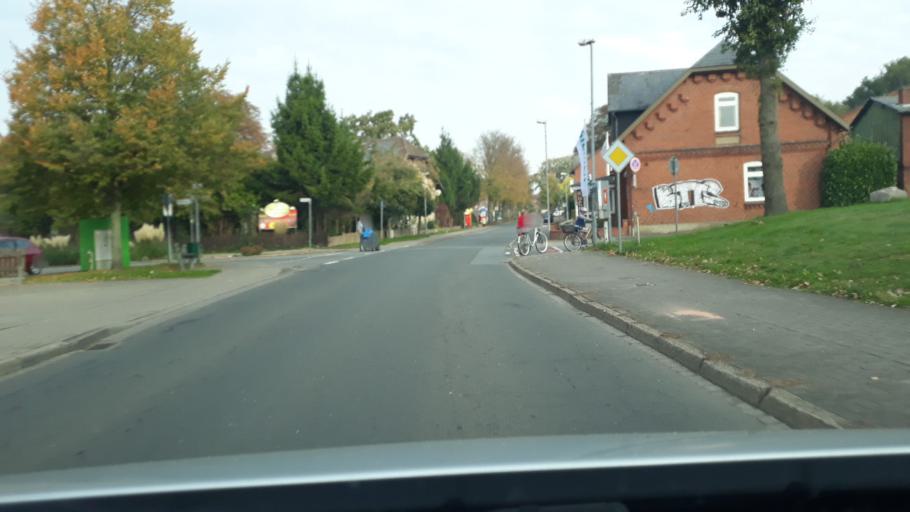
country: DE
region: Schleswig-Holstein
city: Kropp
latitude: 54.4088
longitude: 9.5093
